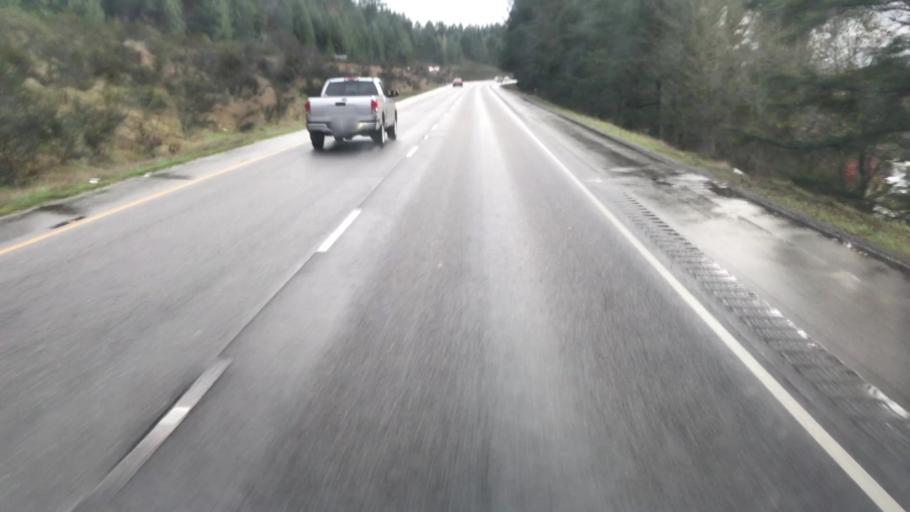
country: US
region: Washington
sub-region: Kitsap County
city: Burley
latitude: 47.4559
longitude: -122.6225
